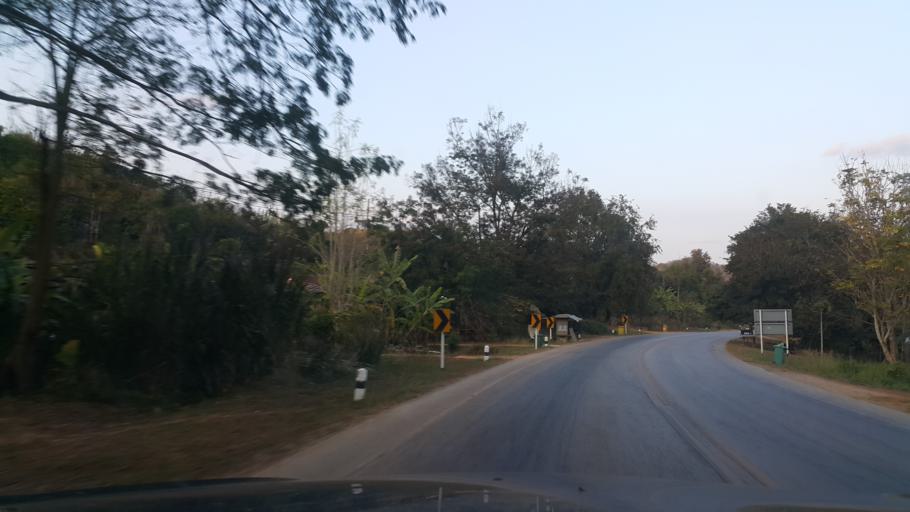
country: TH
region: Loei
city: Loei
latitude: 17.4832
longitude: 101.6077
